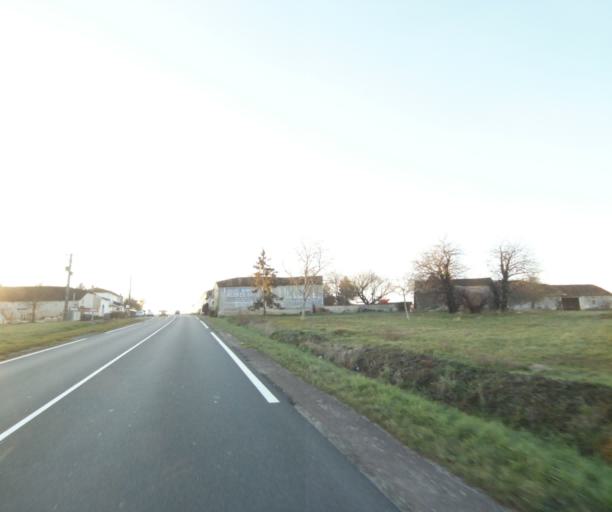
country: FR
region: Poitou-Charentes
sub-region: Departement de la Charente-Maritime
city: Cherac
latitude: 45.7136
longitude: -0.4928
